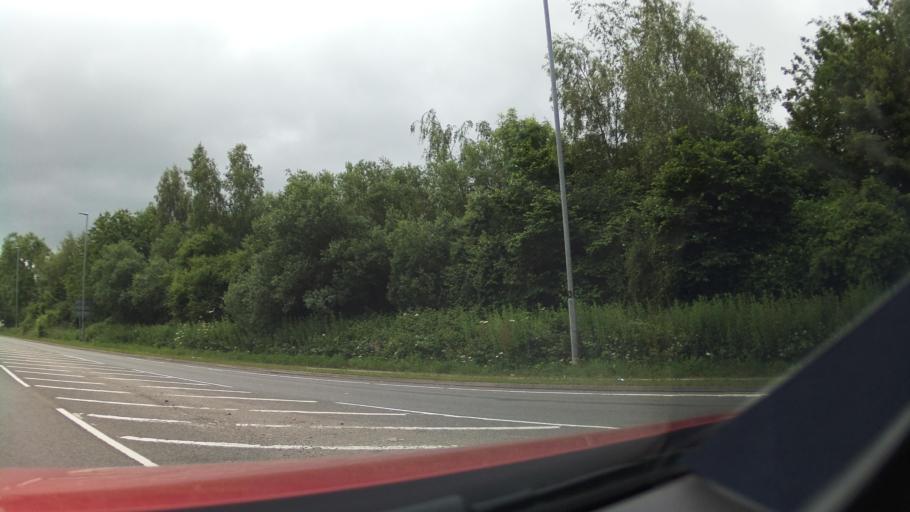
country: GB
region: England
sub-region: Leicestershire
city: Ashby de la Zouch
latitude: 52.7559
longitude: -1.4529
